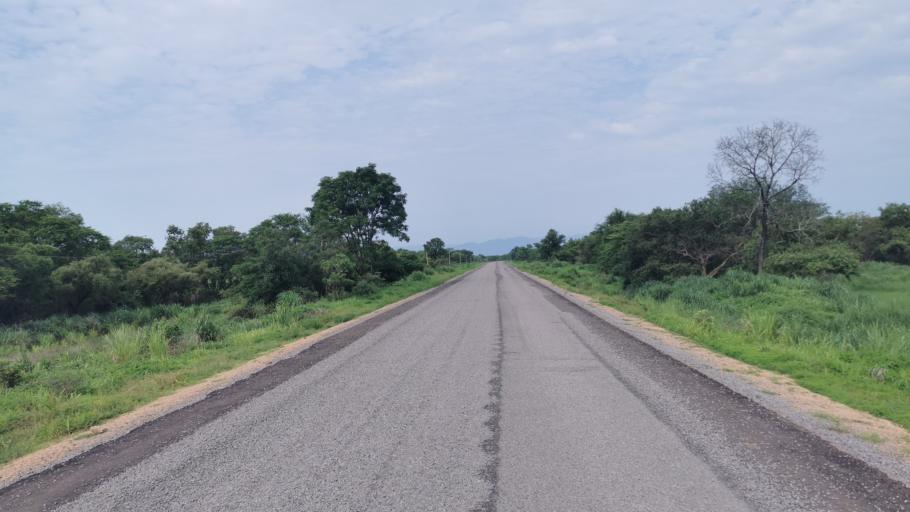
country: ET
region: Gambela
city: Gambela
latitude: 7.8364
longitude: 34.5540
